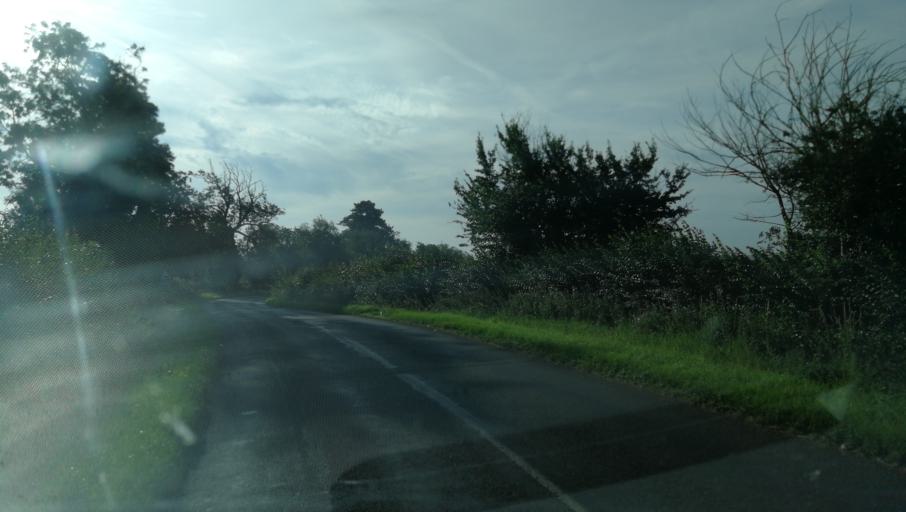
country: GB
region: England
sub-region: Oxfordshire
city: Bloxham
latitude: 52.0234
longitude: -1.3928
